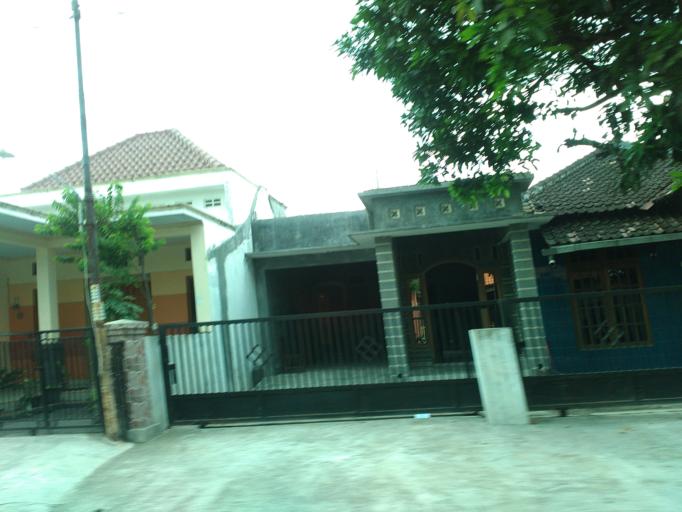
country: ID
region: Central Java
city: Ceper
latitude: -7.6622
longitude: 110.6595
